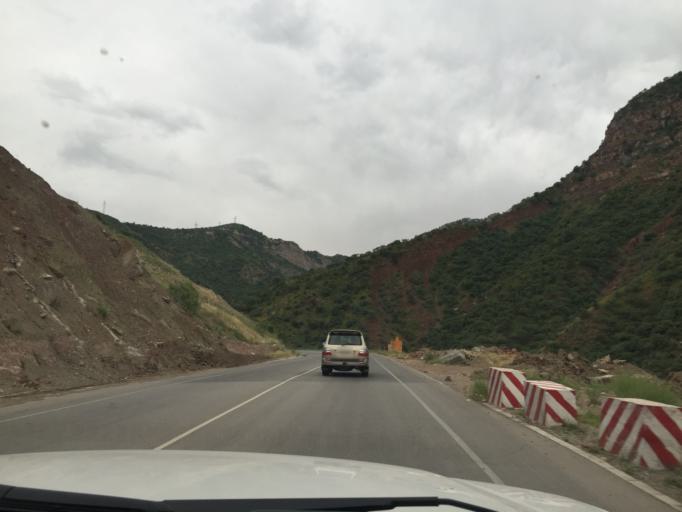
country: TJ
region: Khatlon
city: Norak
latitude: 38.3451
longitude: 69.2382
